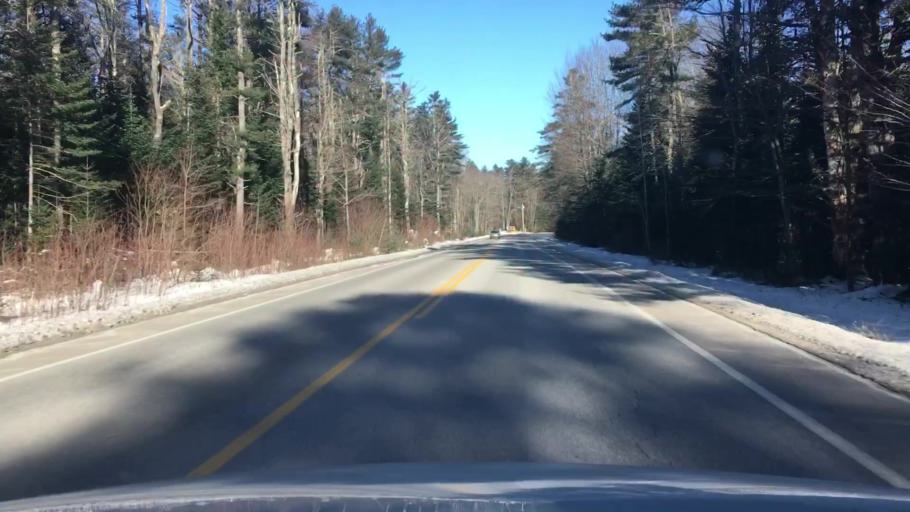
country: US
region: Maine
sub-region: Androscoggin County
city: Lisbon Falls
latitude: 43.9567
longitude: -70.1223
